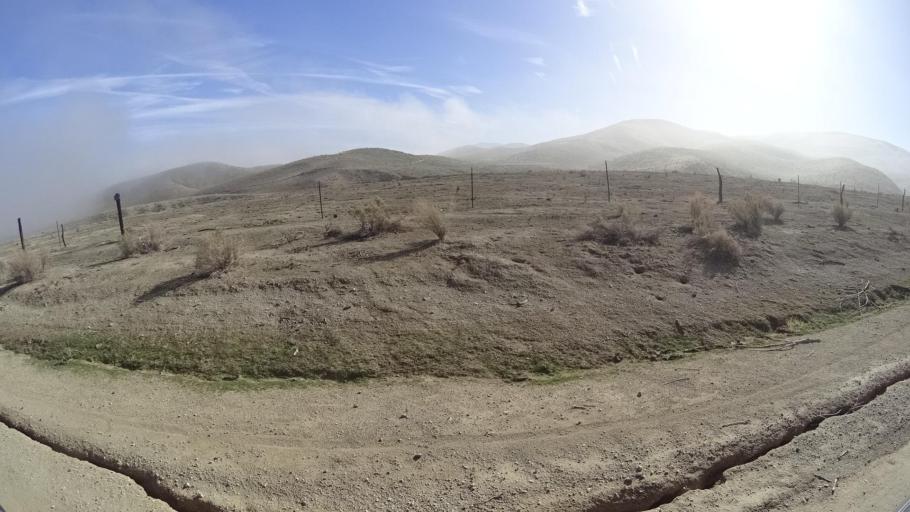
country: US
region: California
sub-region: Kern County
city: Maricopa
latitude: 35.0180
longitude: -119.4504
